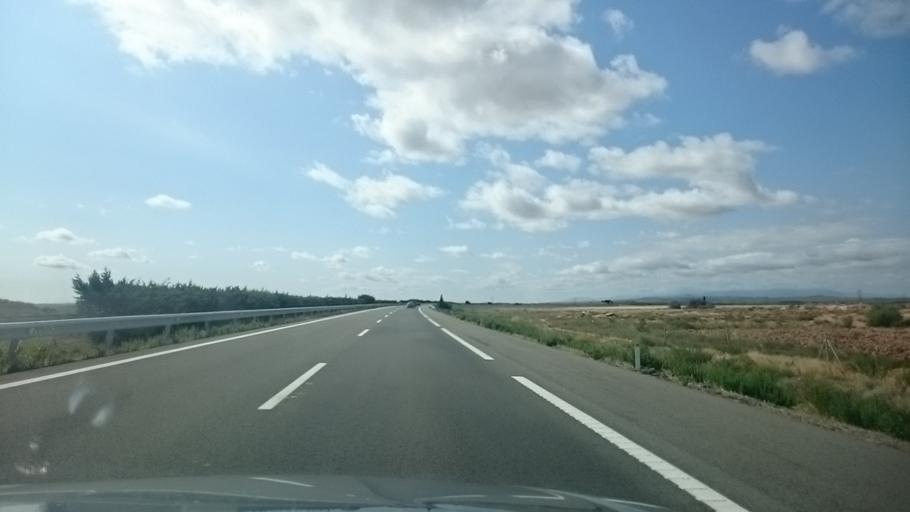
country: ES
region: La Rioja
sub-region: Provincia de La Rioja
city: Rincon de Soto
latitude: 42.1901
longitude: -1.8438
